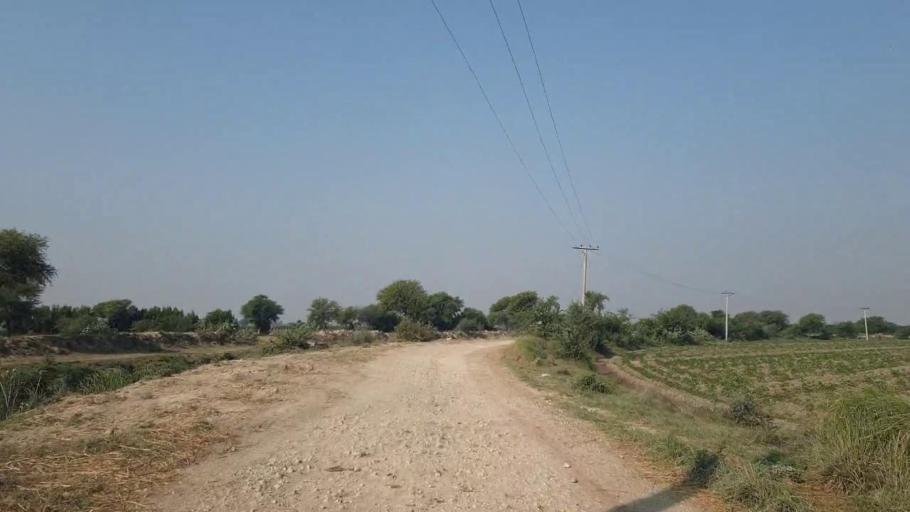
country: PK
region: Sindh
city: Matli
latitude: 24.9894
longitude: 68.6243
